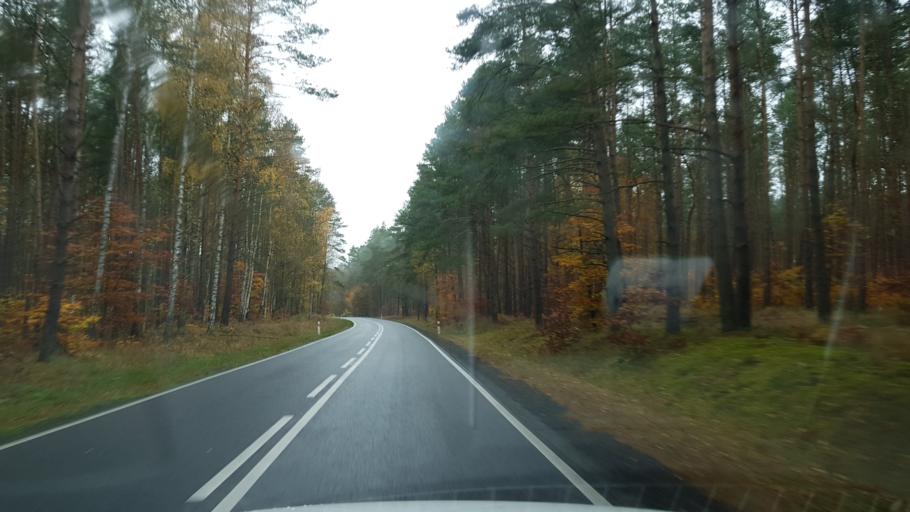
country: PL
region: West Pomeranian Voivodeship
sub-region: Powiat goleniowski
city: Stepnica
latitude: 53.6252
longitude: 14.7225
